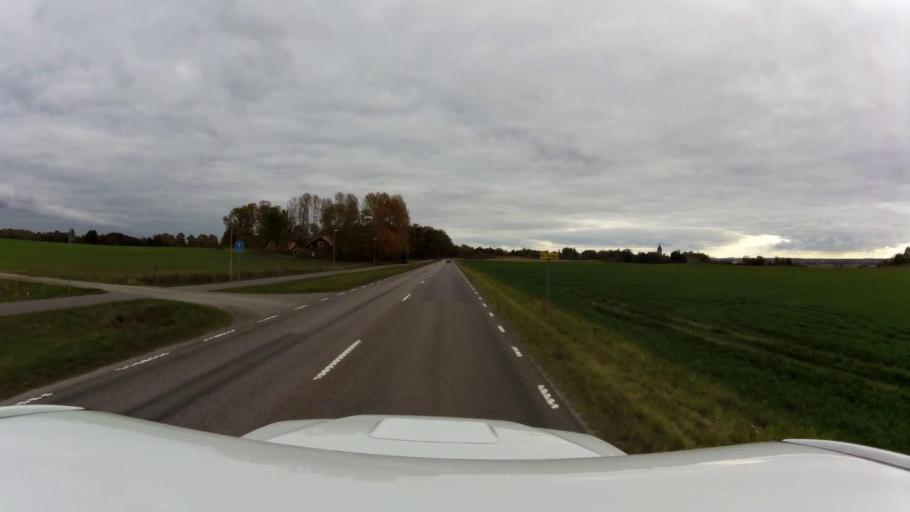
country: SE
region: OEstergoetland
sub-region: Linkopings Kommun
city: Berg
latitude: 58.4885
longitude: 15.5060
